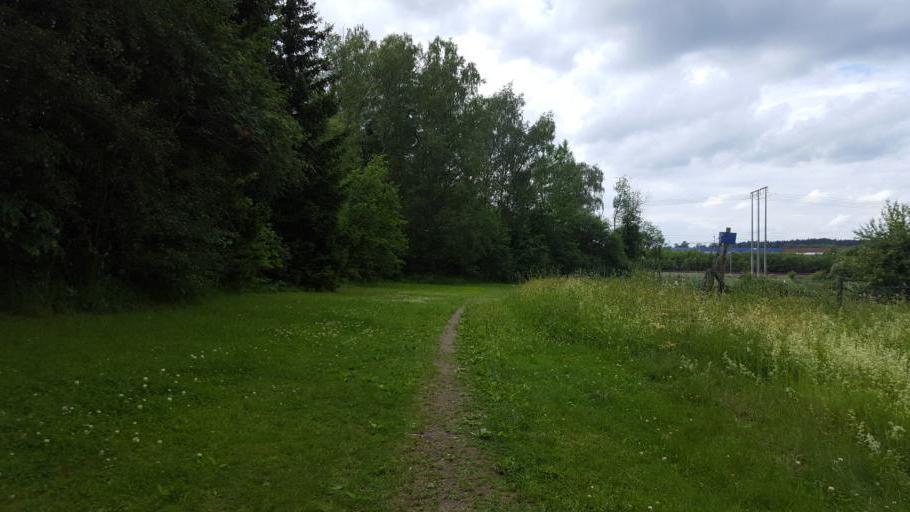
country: SE
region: Stockholm
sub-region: Upplands Vasby Kommun
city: Upplands Vaesby
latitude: 59.5059
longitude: 17.8954
